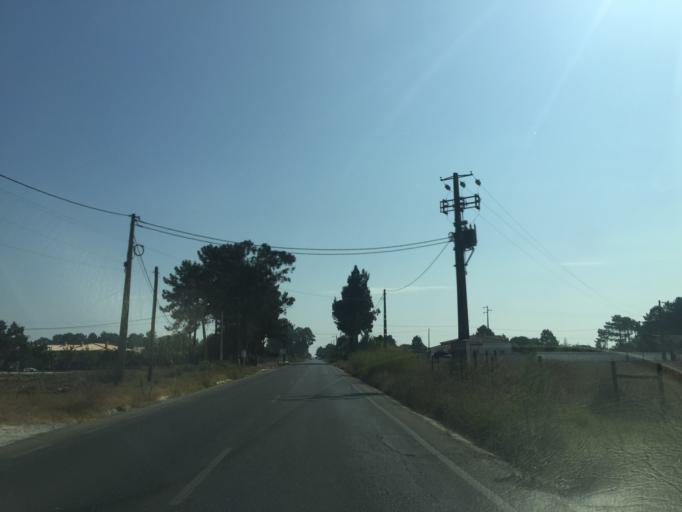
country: PT
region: Santarem
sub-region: Salvaterra de Magos
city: Salvaterra de Magos
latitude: 39.0290
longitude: -8.7569
